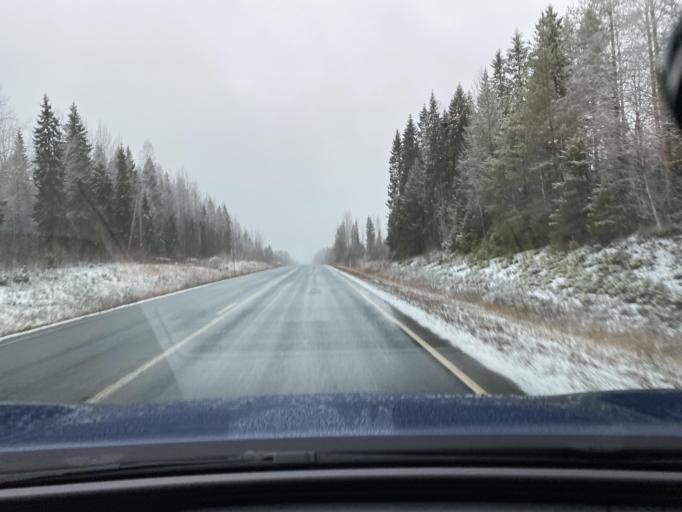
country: FI
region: Northern Ostrobothnia
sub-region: Oulu
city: Kiiminki
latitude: 65.1414
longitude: 25.8641
